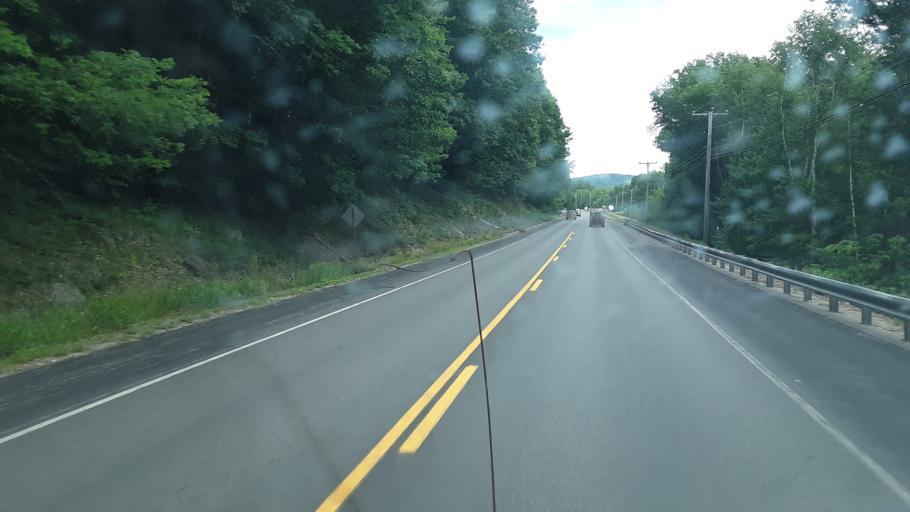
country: US
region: Maine
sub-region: Oxford County
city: Dixfield
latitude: 44.5314
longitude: -70.4881
